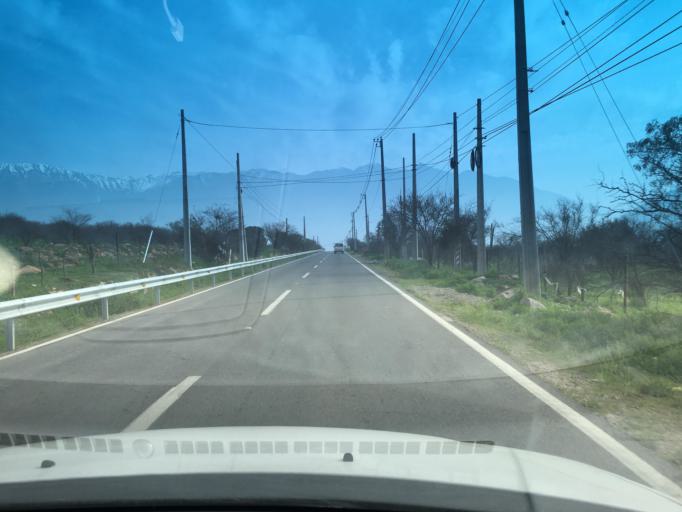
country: CL
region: Santiago Metropolitan
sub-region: Provincia de Chacabuco
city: Lampa
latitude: -33.2546
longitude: -70.9064
